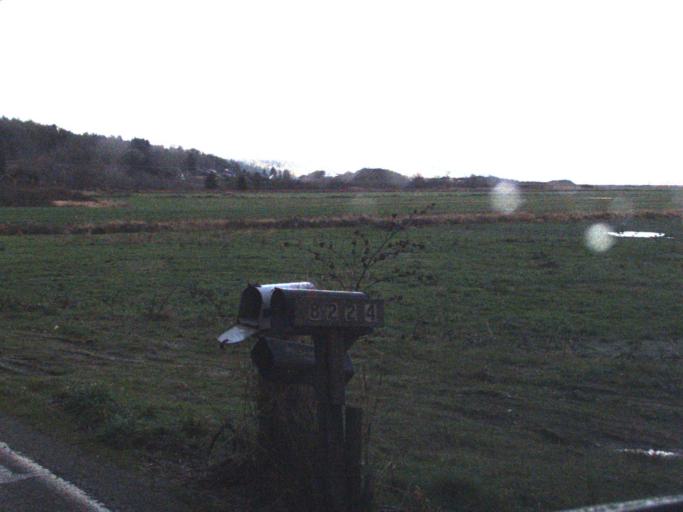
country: US
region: Washington
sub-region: Snohomish County
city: Silver Firs
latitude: 47.8799
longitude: -122.1216
